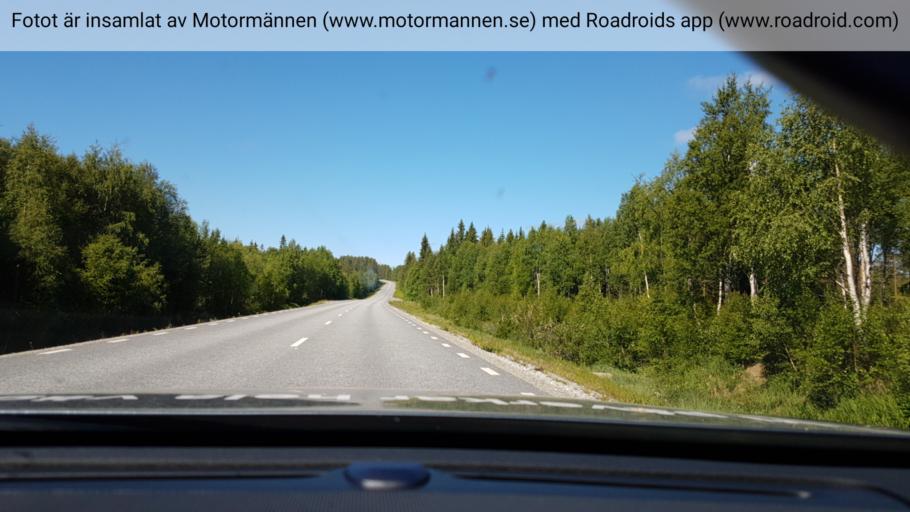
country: SE
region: Vaesterbotten
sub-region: Asele Kommun
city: Asele
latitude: 64.1998
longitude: 17.5337
